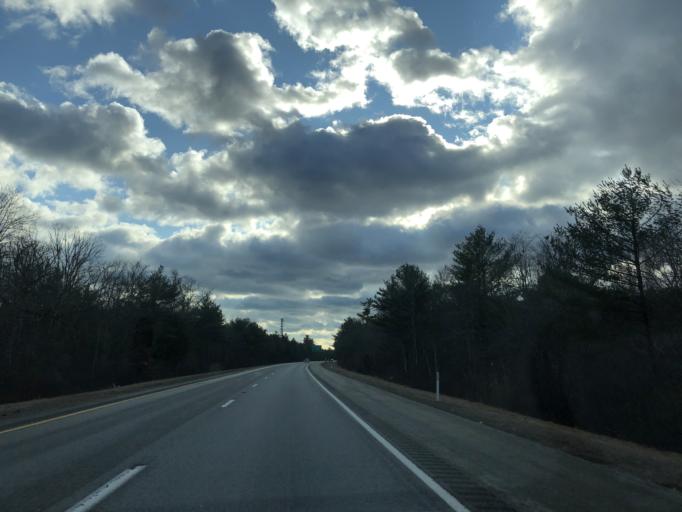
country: US
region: Massachusetts
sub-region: Plymouth County
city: Mattapoisett Center
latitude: 41.6939
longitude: -70.8034
